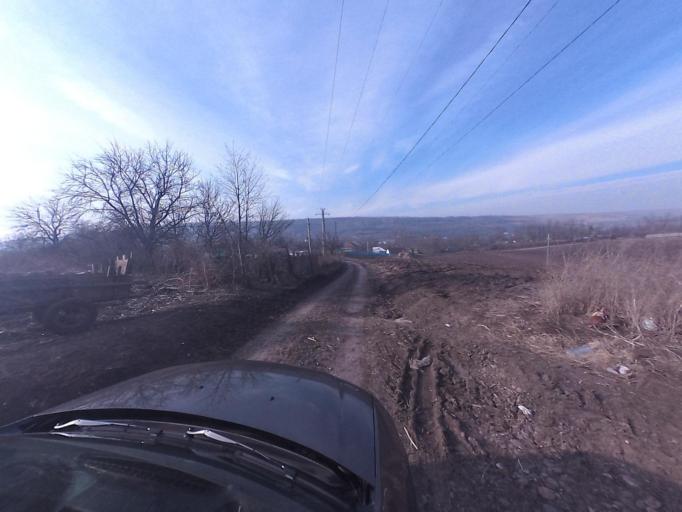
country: RO
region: Vaslui
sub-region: Comuna Solesti
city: Solesti
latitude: 46.8117
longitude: 27.7778
